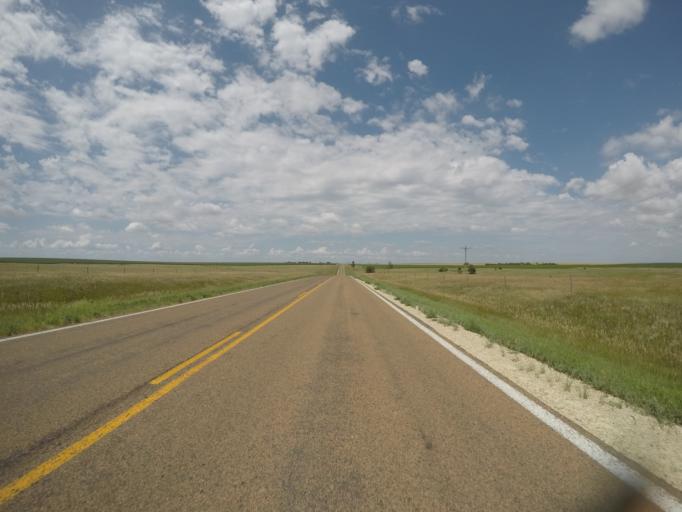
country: US
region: Kansas
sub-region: Rawlins County
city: Atwood
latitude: 39.9656
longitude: -101.0562
